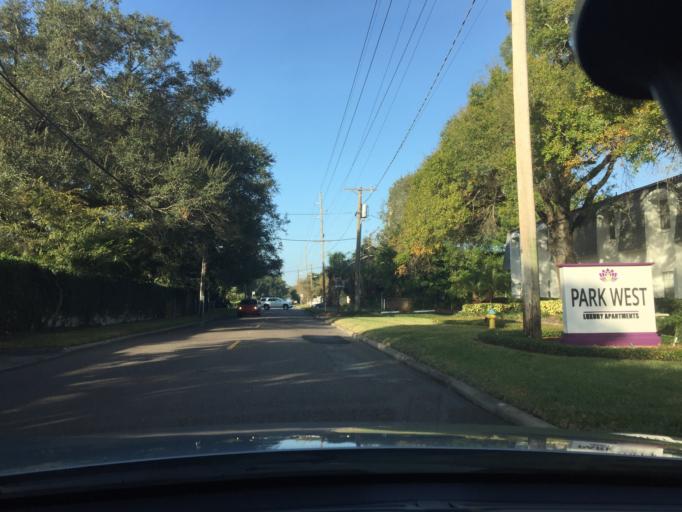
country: US
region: Florida
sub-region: Hillsborough County
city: Tampa
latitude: 27.9375
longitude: -82.4965
